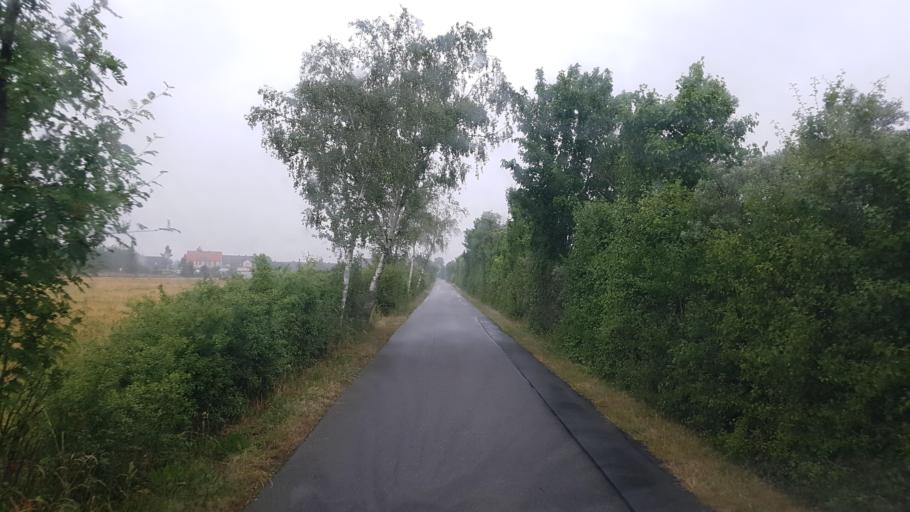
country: DE
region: Brandenburg
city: Muhlberg
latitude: 51.4613
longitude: 13.2993
